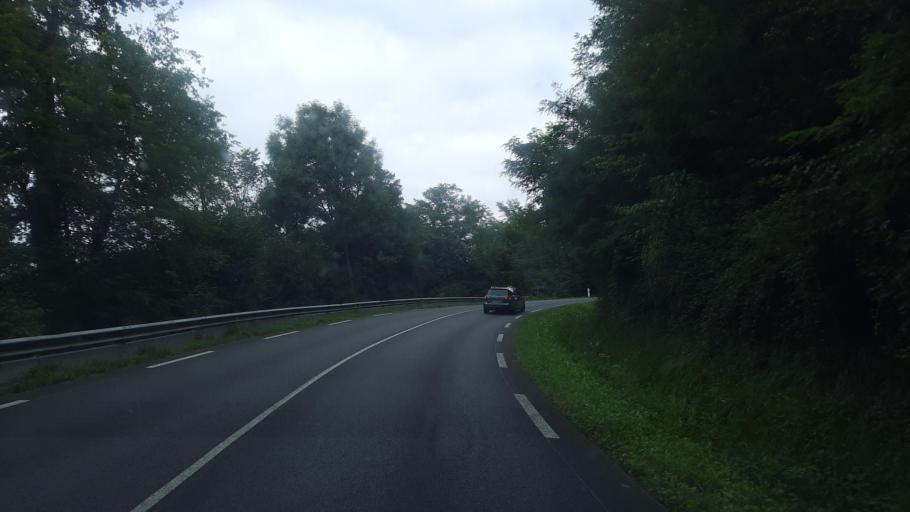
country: FR
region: Midi-Pyrenees
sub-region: Departement des Hautes-Pyrenees
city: Semeac
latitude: 43.2391
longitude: 0.1163
